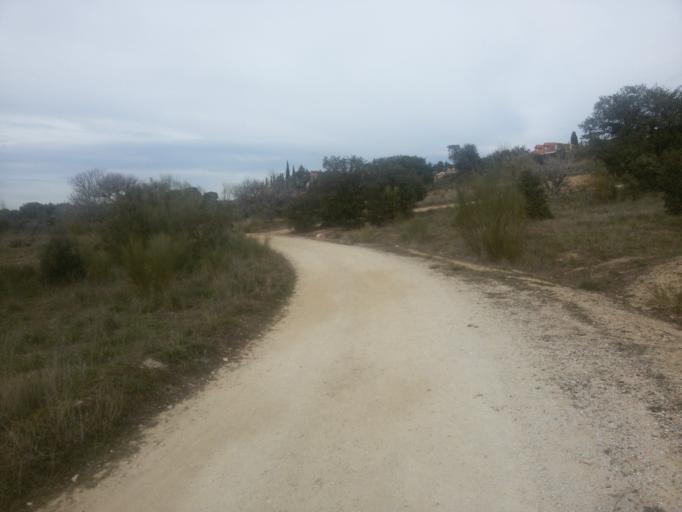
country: ES
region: Madrid
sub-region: Provincia de Madrid
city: Sevilla La Nueva
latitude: 40.3390
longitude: -4.0283
